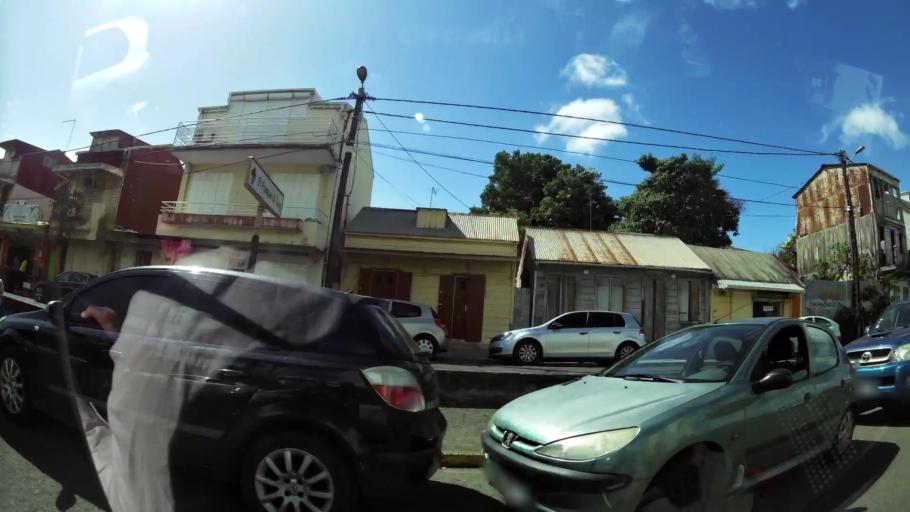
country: GP
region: Guadeloupe
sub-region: Guadeloupe
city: Pointe-a-Pitre
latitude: 16.2396
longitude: -61.5313
